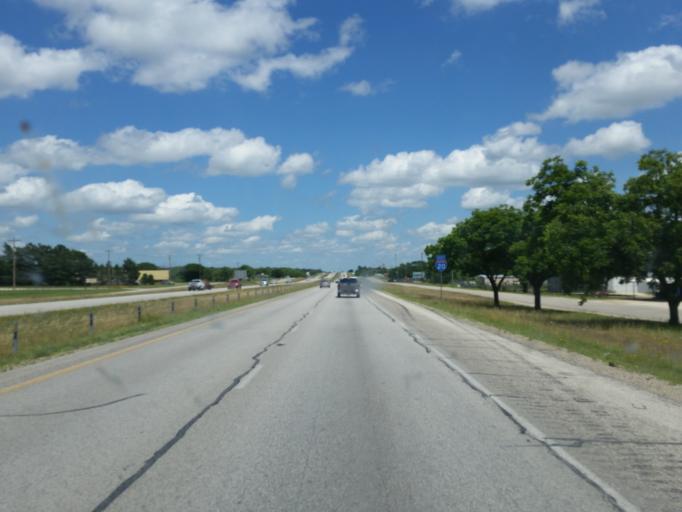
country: US
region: Texas
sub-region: Callahan County
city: Clyde
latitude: 32.4108
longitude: -99.4817
